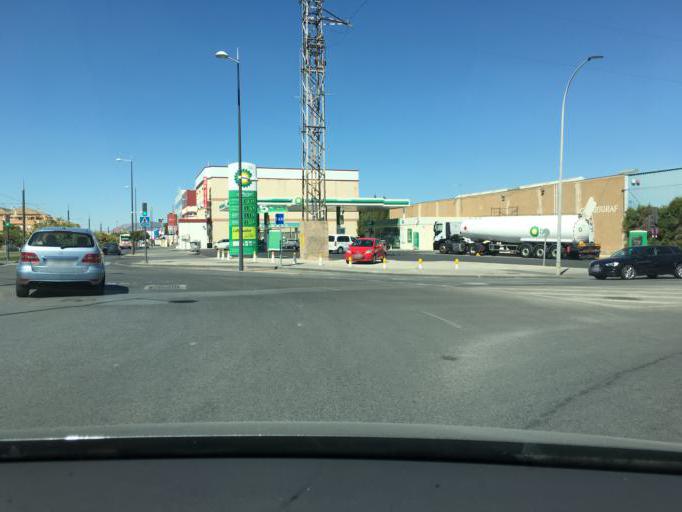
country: ES
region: Andalusia
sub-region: Provincia de Granada
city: Albolote
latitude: 37.2229
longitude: -3.6459
